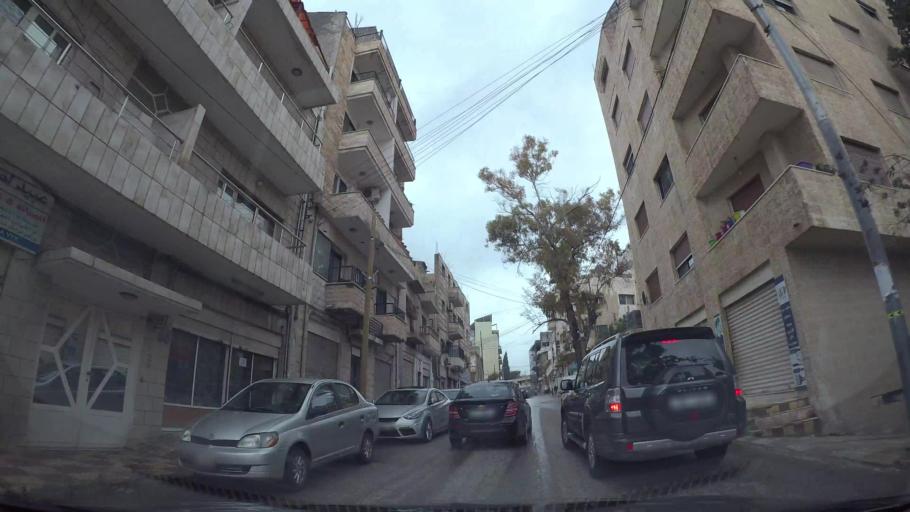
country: JO
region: Amman
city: Amman
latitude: 31.9474
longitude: 35.9282
